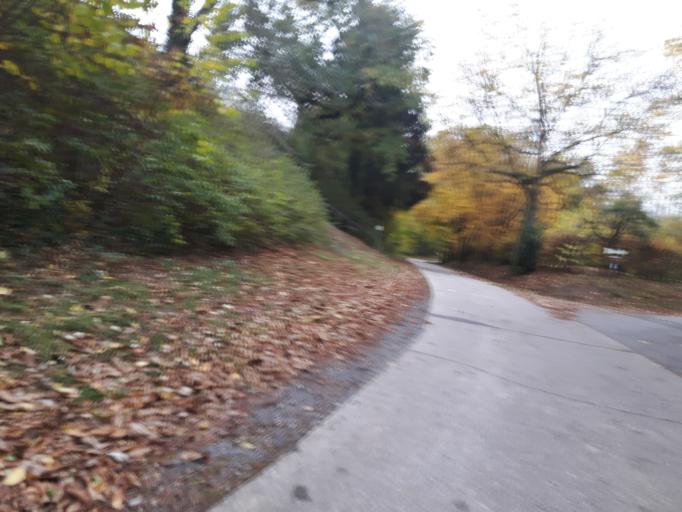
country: DE
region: Baden-Wuerttemberg
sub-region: Karlsruhe Region
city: Zaisenhausen
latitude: 49.1725
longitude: 8.7970
